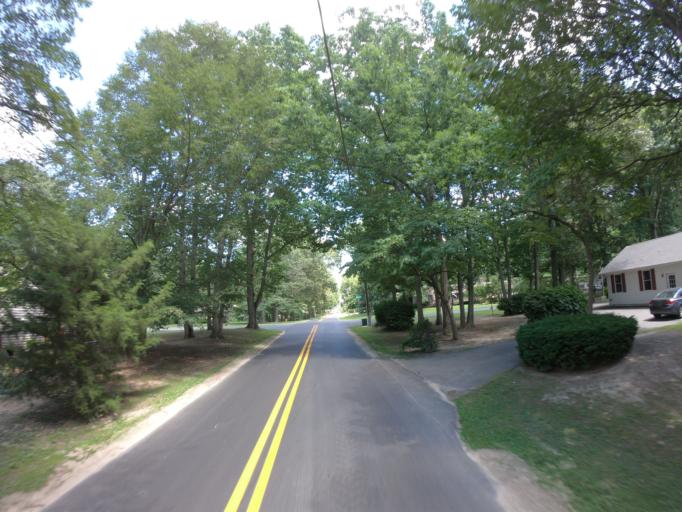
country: US
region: Delaware
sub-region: Sussex County
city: Milford
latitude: 38.9311
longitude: -75.4169
